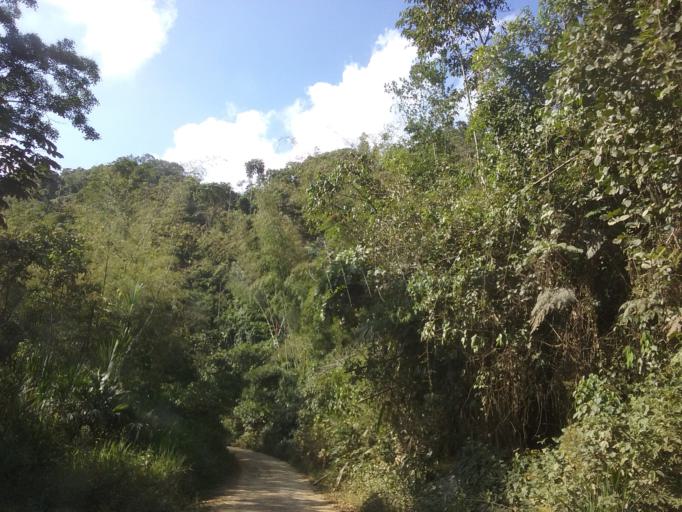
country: CO
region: Tolima
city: Libano
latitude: 4.8955
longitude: -75.0274
